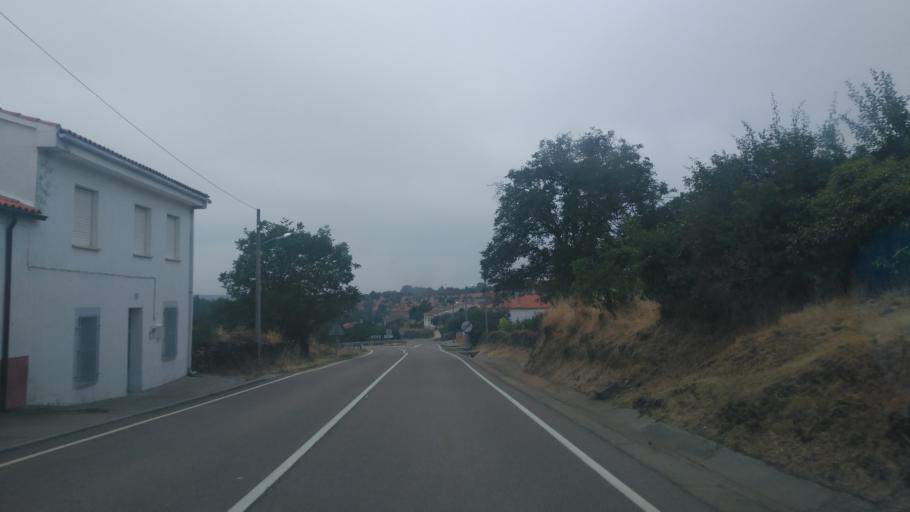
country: ES
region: Castille and Leon
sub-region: Provincia de Salamanca
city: Cereceda de la Sierra
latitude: 40.5646
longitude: -6.0909
